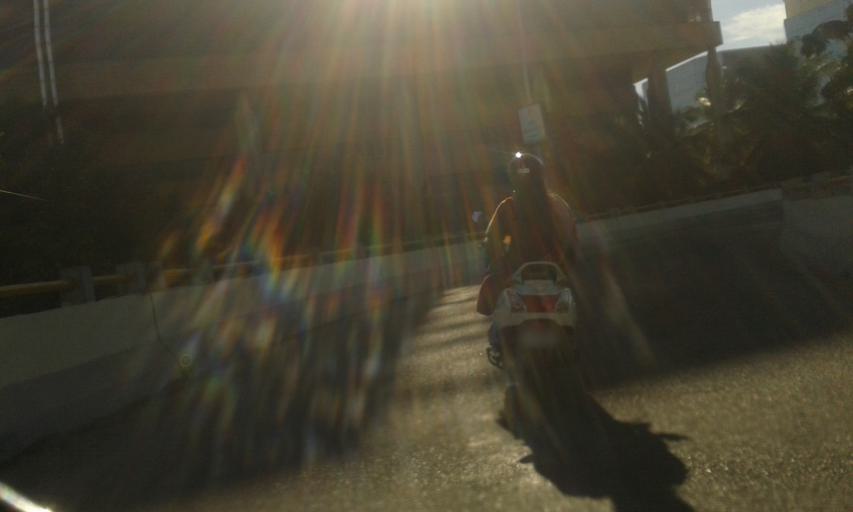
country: IN
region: Karnataka
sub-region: Bangalore Urban
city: Bangalore
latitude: 12.9611
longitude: 77.6431
